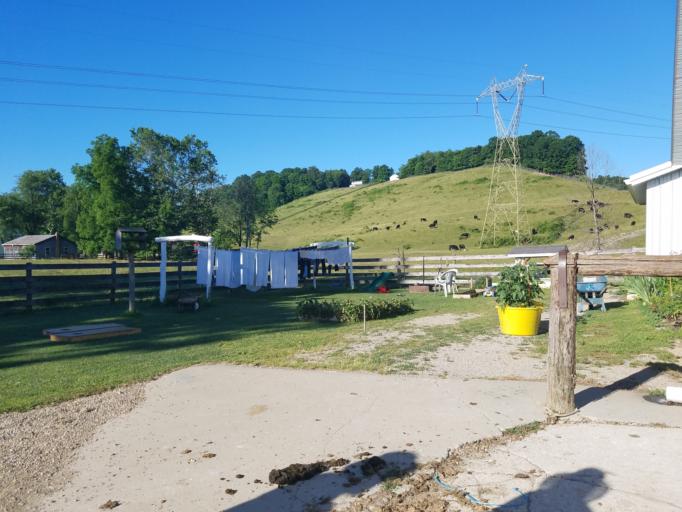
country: US
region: Ohio
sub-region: Columbiana County
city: Salineville
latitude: 40.5247
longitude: -80.8392
